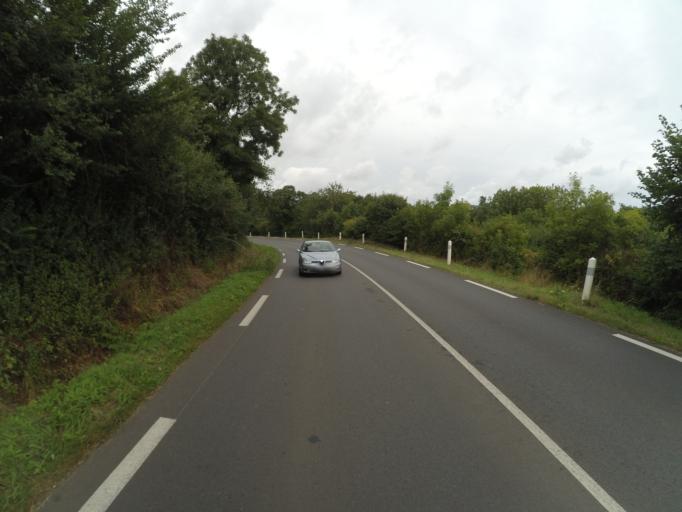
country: FR
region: Brittany
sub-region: Departement des Cotes-d'Armor
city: Tremuson
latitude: 48.5223
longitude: -2.8167
